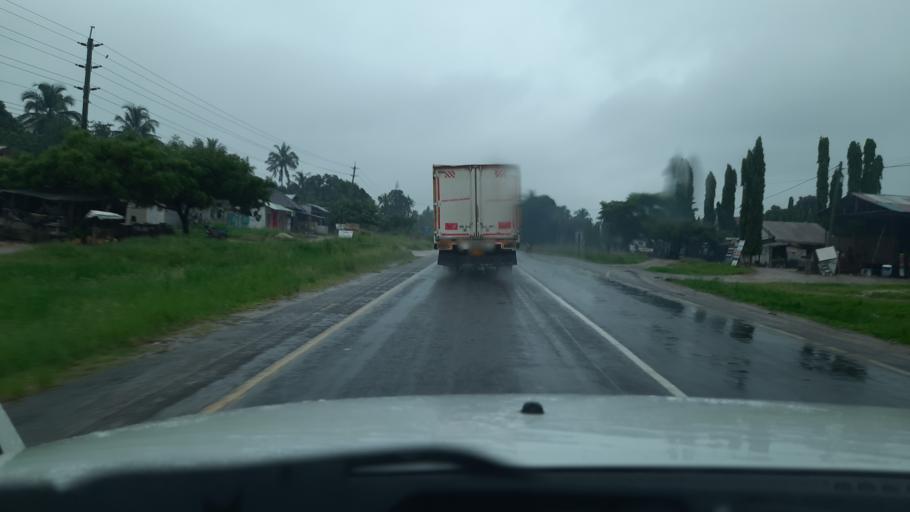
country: TZ
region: Pwani
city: Bagamoyo
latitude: -6.5836
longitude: 39.0384
